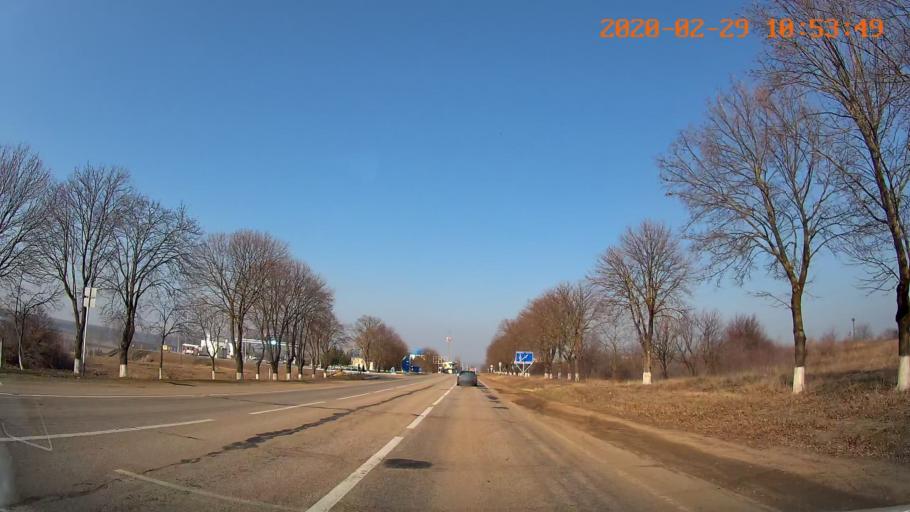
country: MD
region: Telenesti
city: Grigoriopol
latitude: 47.1186
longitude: 29.3308
